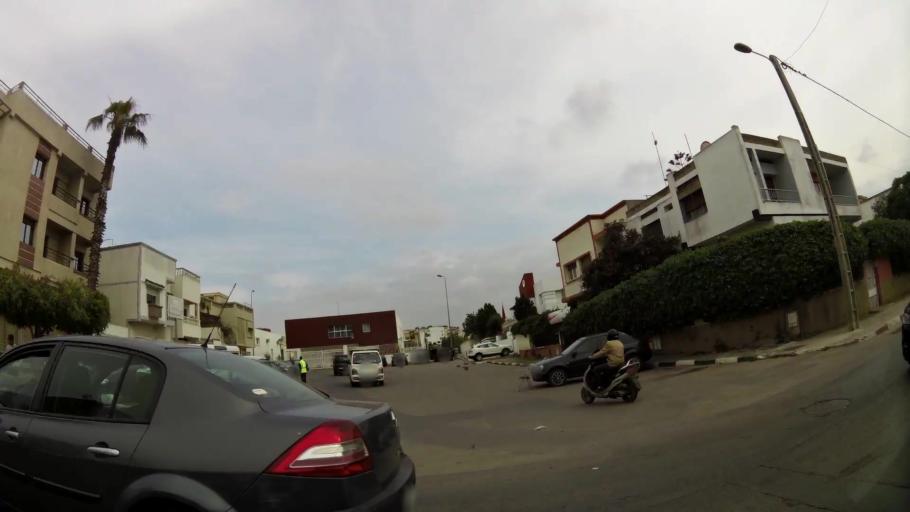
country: MA
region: Rabat-Sale-Zemmour-Zaer
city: Sale
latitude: 34.0306
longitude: -6.8093
